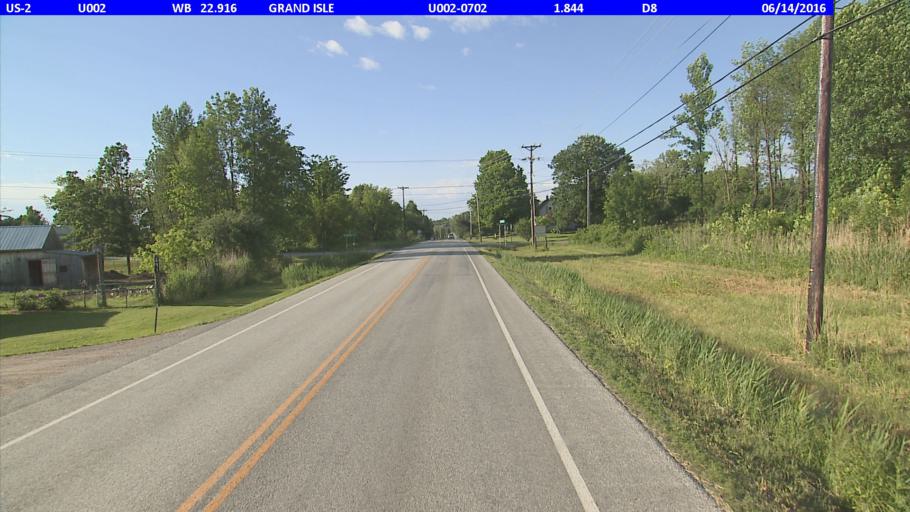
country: US
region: Vermont
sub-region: Grand Isle County
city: North Hero
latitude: 44.7409
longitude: -73.2895
